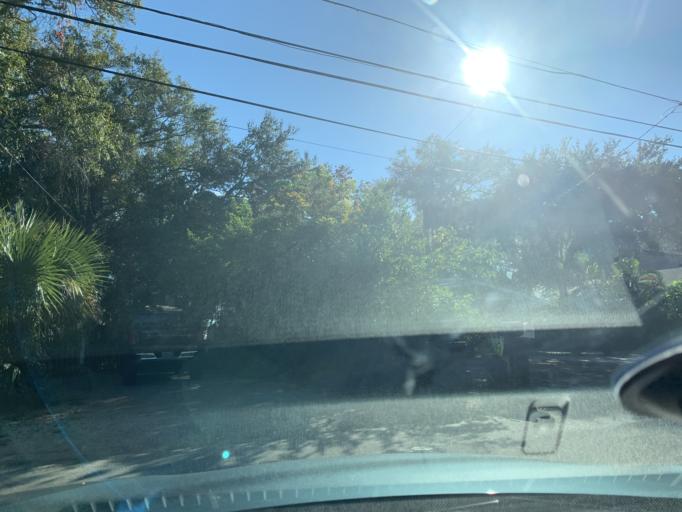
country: US
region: Florida
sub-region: Pinellas County
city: Gulfport
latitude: 27.7389
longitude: -82.7022
